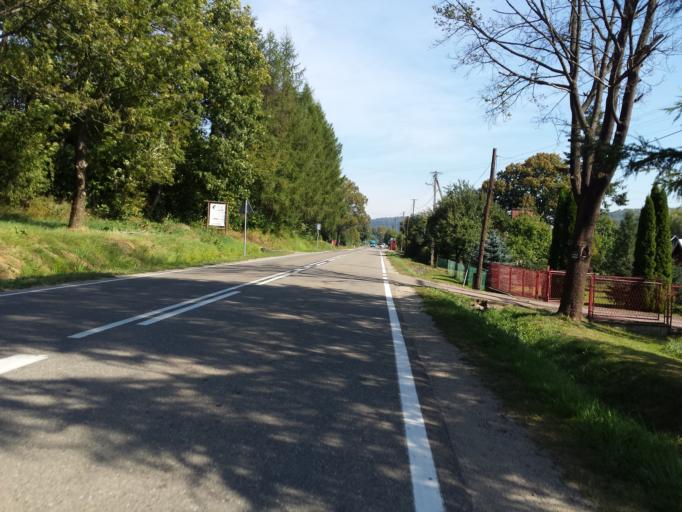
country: PL
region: Subcarpathian Voivodeship
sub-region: Powiat leski
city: Baligrod
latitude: 49.3283
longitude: 22.2846
